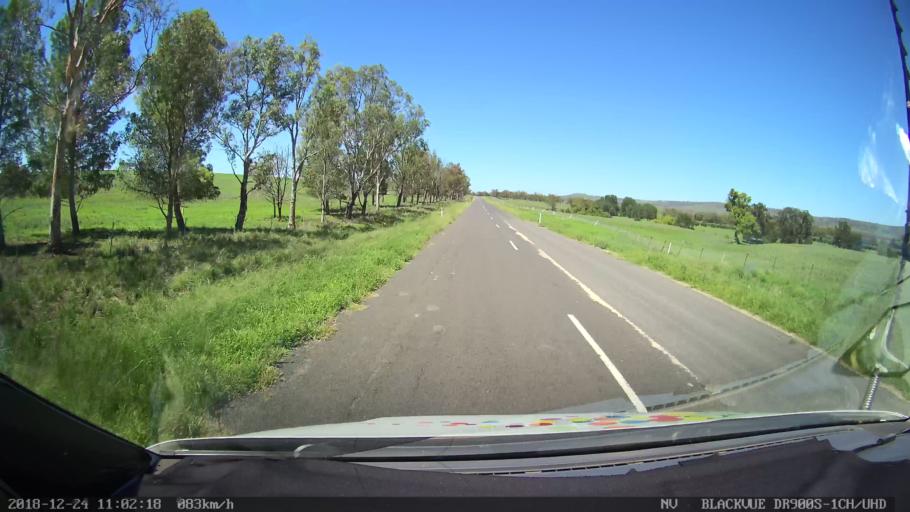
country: AU
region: New South Wales
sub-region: Upper Hunter Shire
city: Merriwa
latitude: -32.0835
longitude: 150.3763
